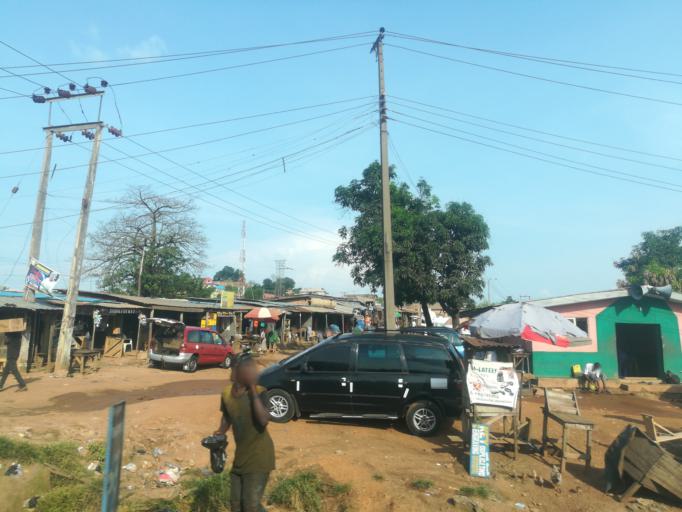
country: NG
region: Oyo
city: Moniya
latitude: 7.4770
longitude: 3.9137
